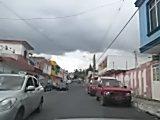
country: MX
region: Nayarit
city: Tepic
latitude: 21.4975
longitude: -104.9049
